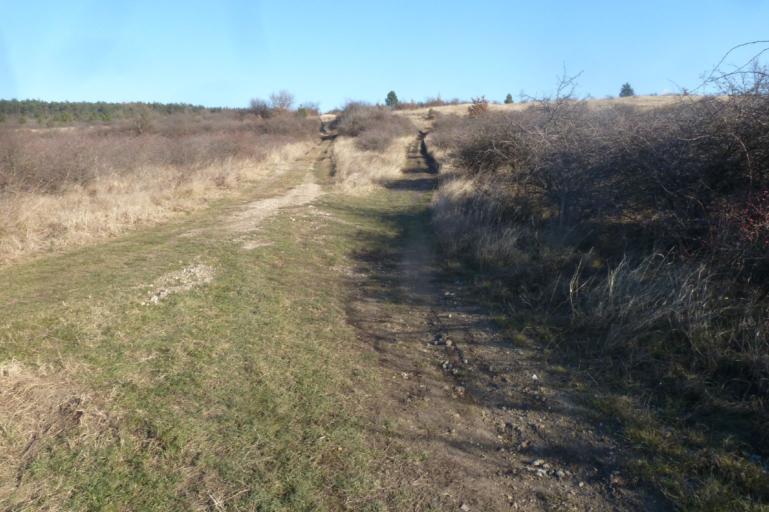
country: HU
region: Pest
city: Soskut
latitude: 47.4271
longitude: 18.8420
